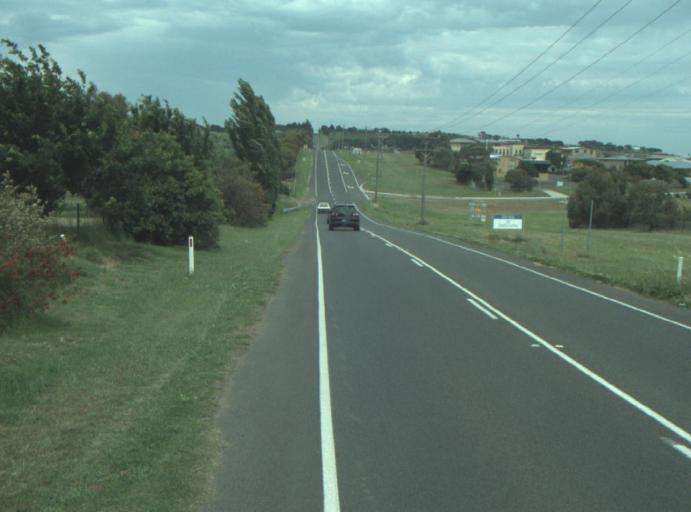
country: AU
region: Victoria
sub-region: Greater Geelong
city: Clifton Springs
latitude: -38.1235
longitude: 144.6335
